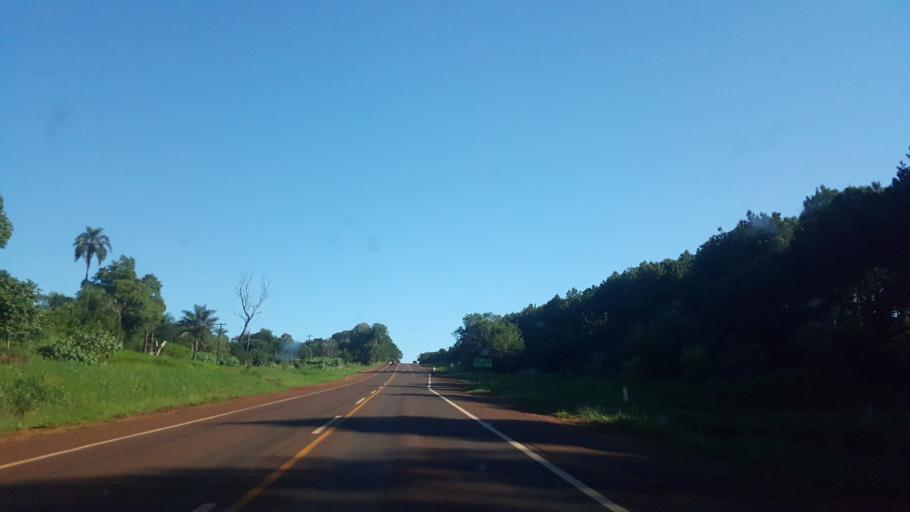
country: AR
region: Misiones
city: Puerto Esperanza
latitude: -26.1556
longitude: -54.5831
